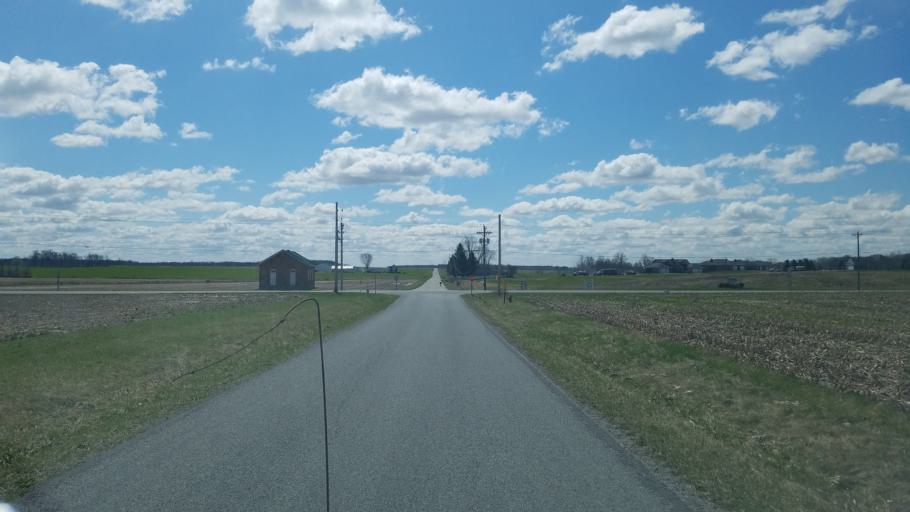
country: US
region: Ohio
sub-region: Seneca County
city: Fostoria
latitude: 41.0664
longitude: -83.5149
